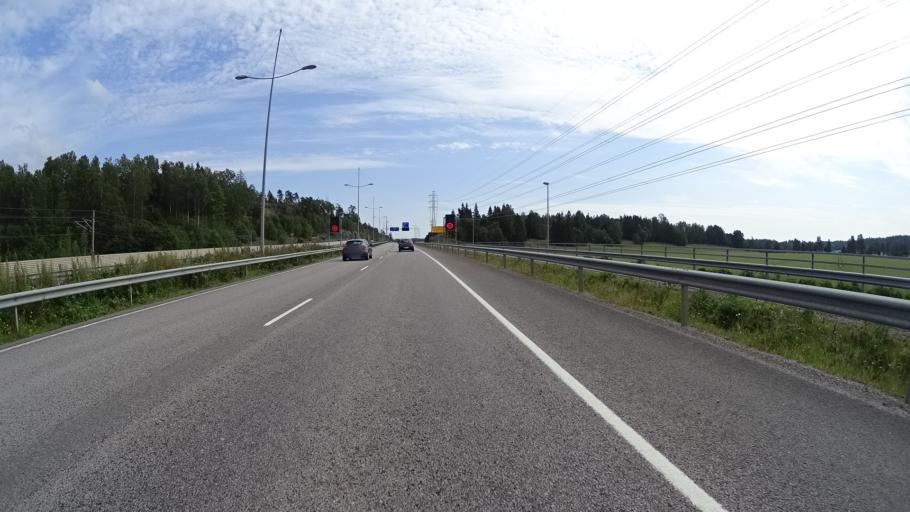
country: FI
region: Uusimaa
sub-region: Helsinki
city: Vantaa
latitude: 60.2495
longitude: 25.1368
